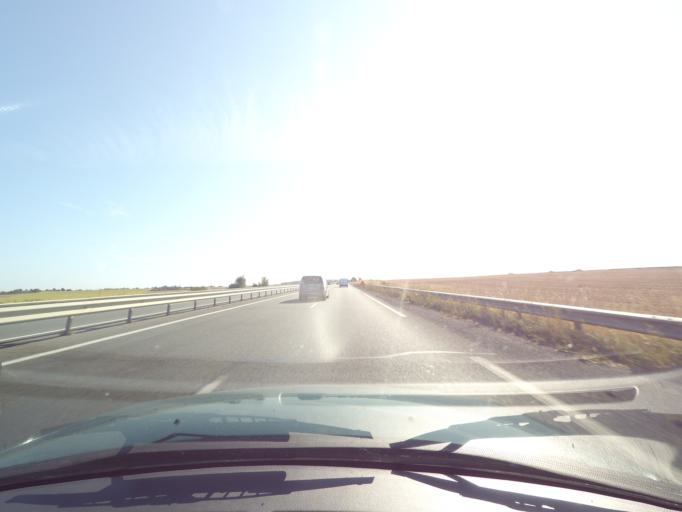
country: FR
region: Poitou-Charentes
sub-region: Departement de la Vienne
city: Migne-Auxances
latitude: 46.6170
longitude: 0.3247
